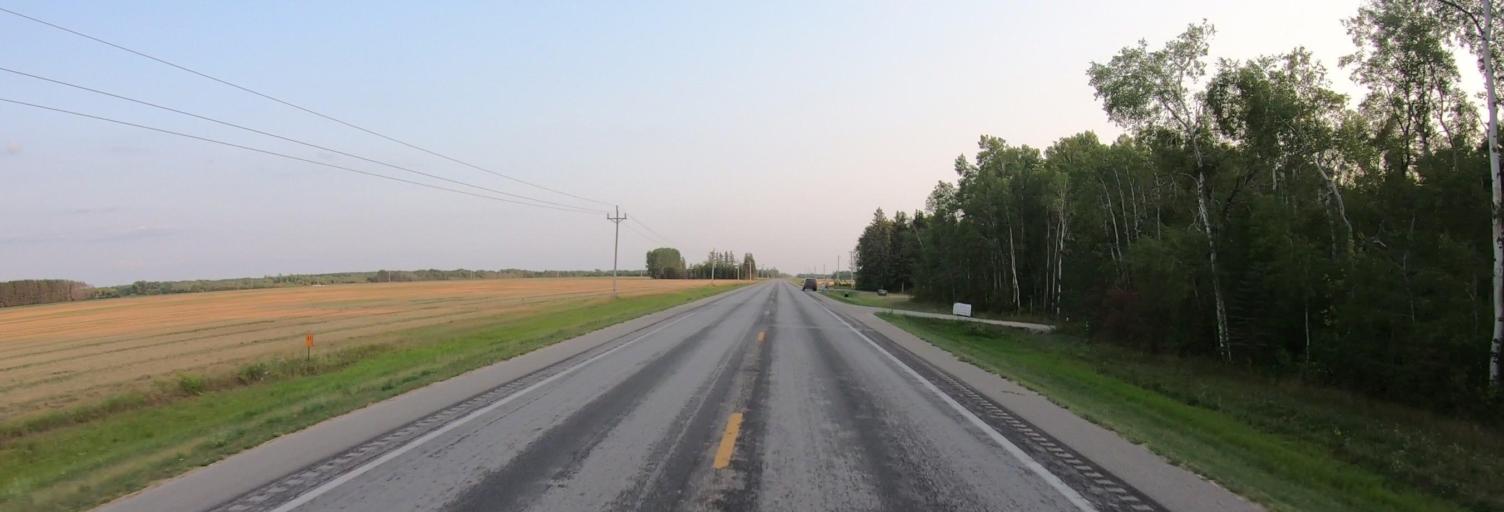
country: US
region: Minnesota
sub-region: Roseau County
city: Warroad
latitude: 48.8640
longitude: -95.3305
